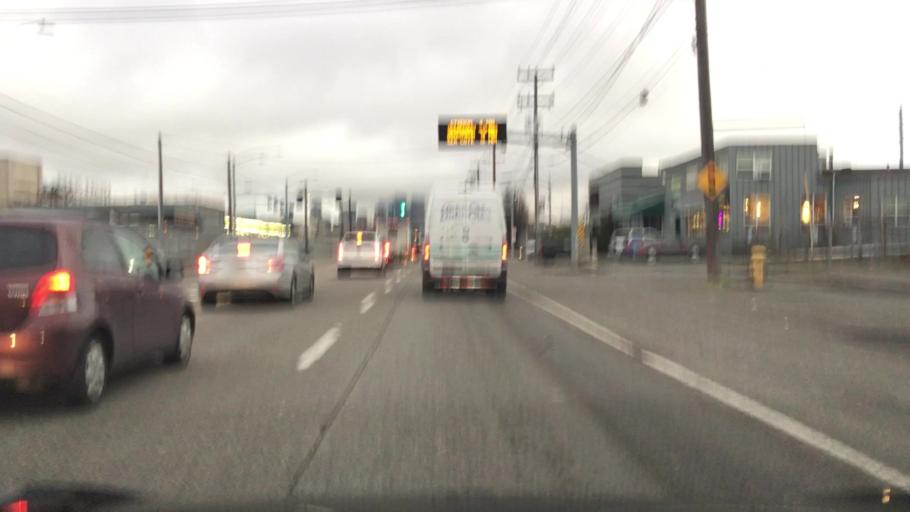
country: US
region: Washington
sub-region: King County
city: Seattle
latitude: 47.5687
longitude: -122.3290
